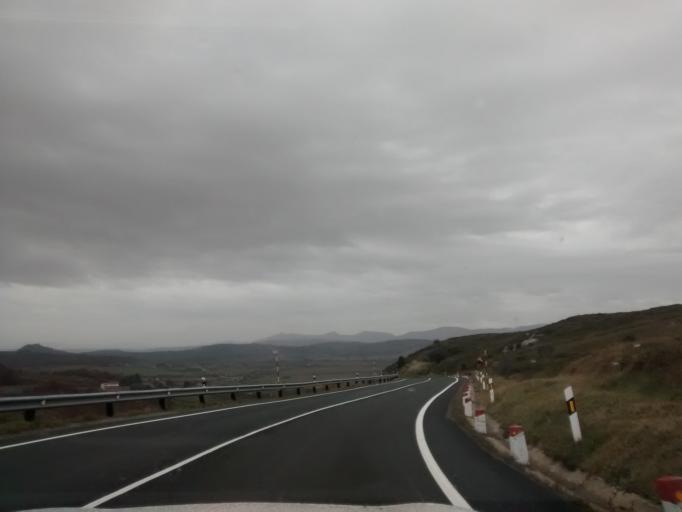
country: ES
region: Castille and Leon
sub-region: Provincia de Burgos
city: Arija
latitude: 43.0364
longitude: -3.8675
